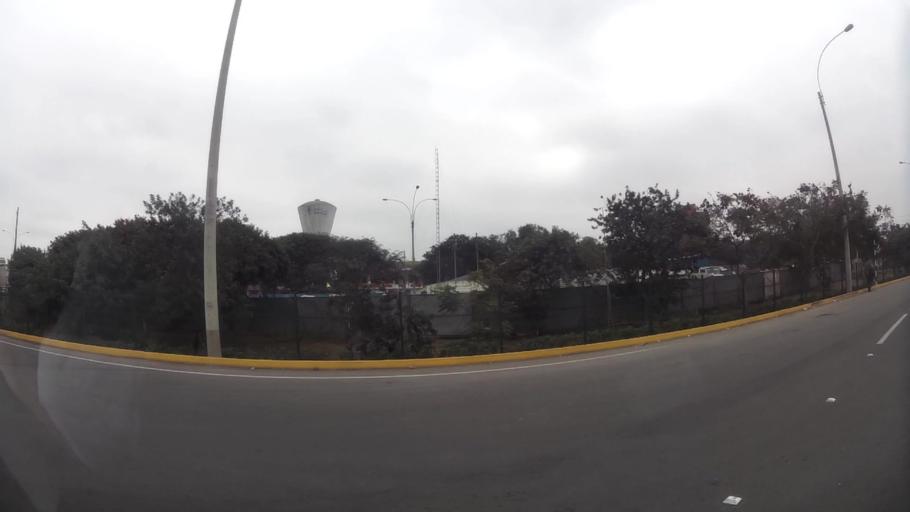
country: PE
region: Lima
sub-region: Lima
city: Independencia
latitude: -11.9774
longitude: -77.0669
